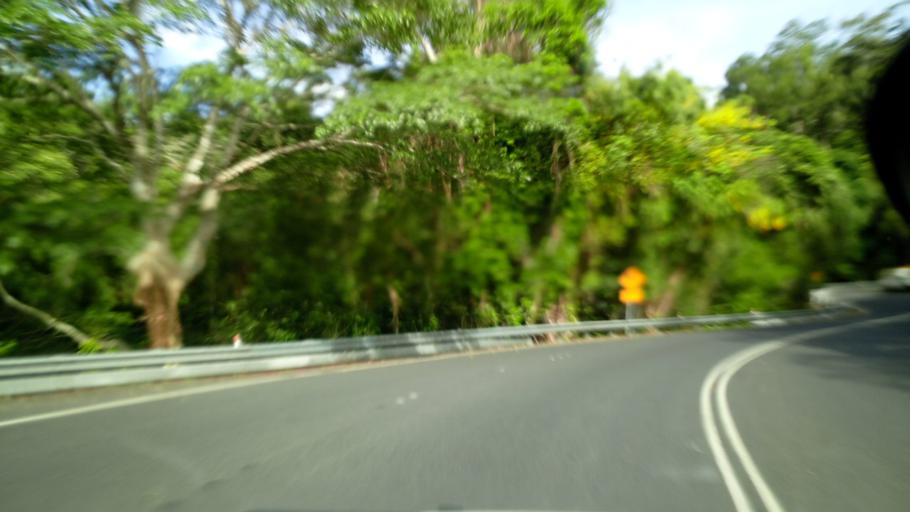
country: AU
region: Queensland
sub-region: Cairns
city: Redlynch
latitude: -16.8417
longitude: 145.6811
